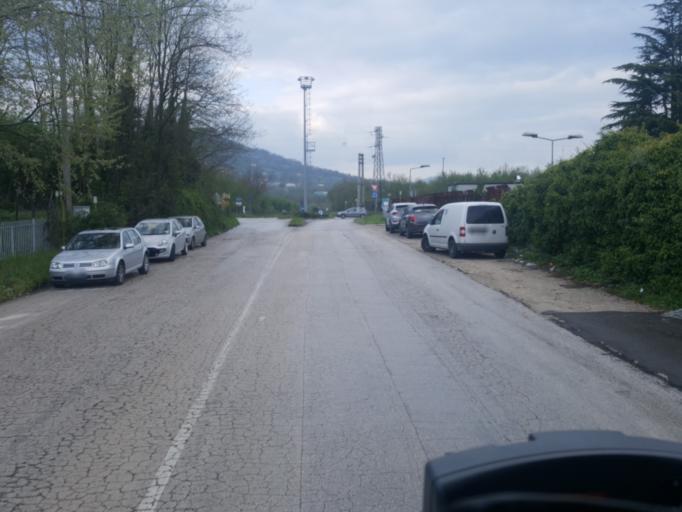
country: IT
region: Campania
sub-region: Provincia di Avellino
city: Atripalda
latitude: 40.9375
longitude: 14.8208
